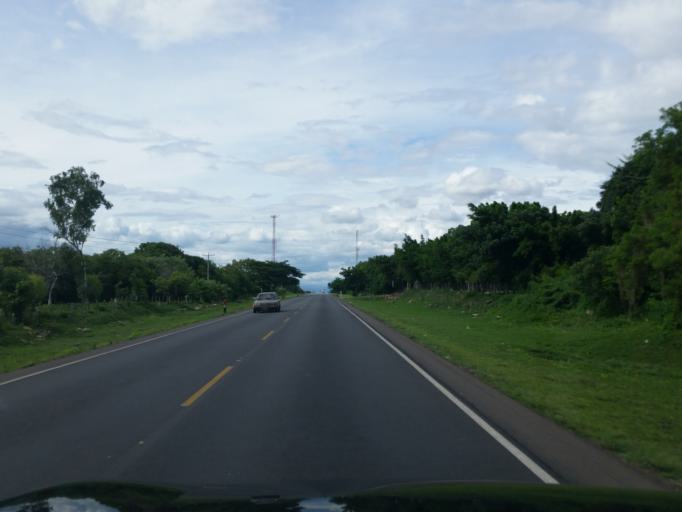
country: NI
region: Matagalpa
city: Ciudad Dario
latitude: 12.7787
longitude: -86.1246
